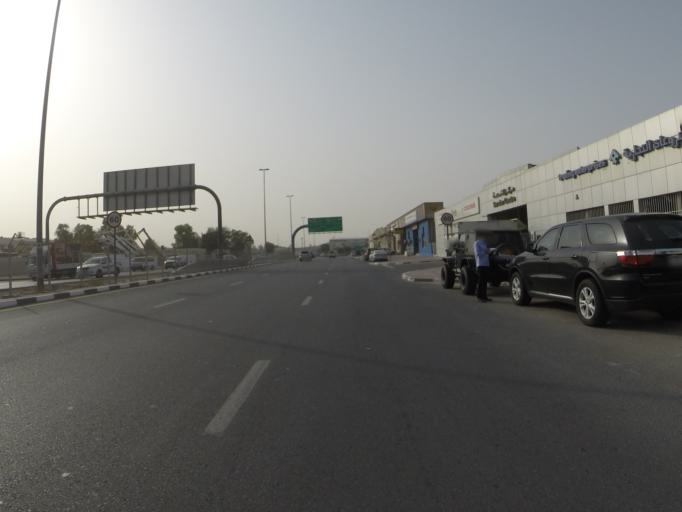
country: AE
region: Dubai
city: Dubai
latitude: 25.1465
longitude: 55.2282
